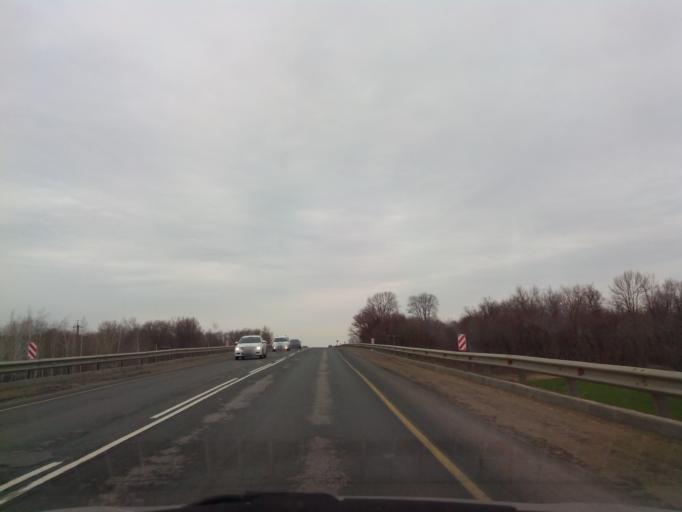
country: RU
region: Tambov
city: Zavoronezhskoye
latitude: 52.9147
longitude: 40.6282
